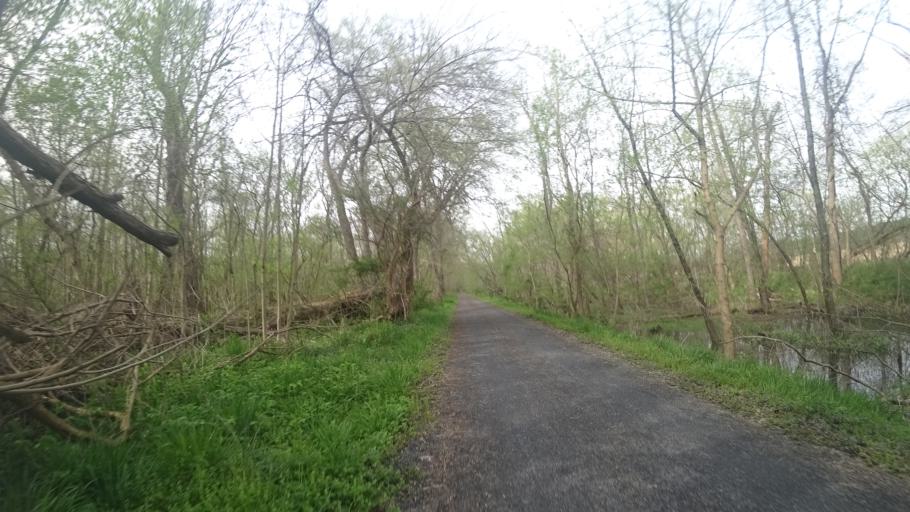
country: US
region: Virginia
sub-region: Loudoun County
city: Leesburg
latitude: 39.1626
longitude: -77.5156
